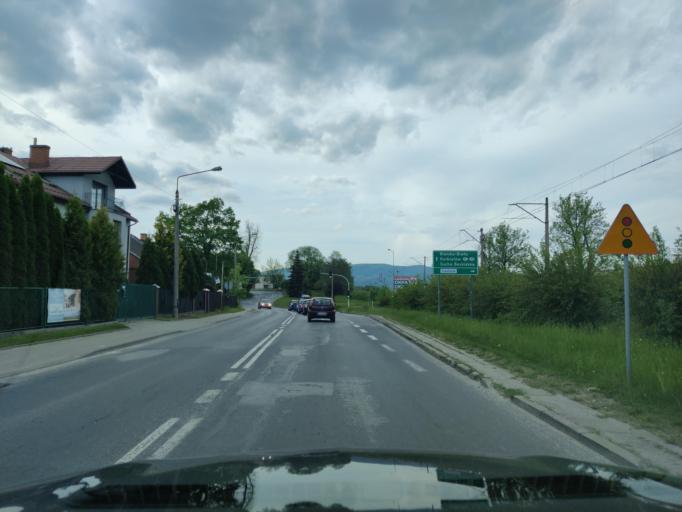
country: PL
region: Silesian Voivodeship
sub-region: Powiat zywiecki
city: Zywiec
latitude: 49.6844
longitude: 19.1868
